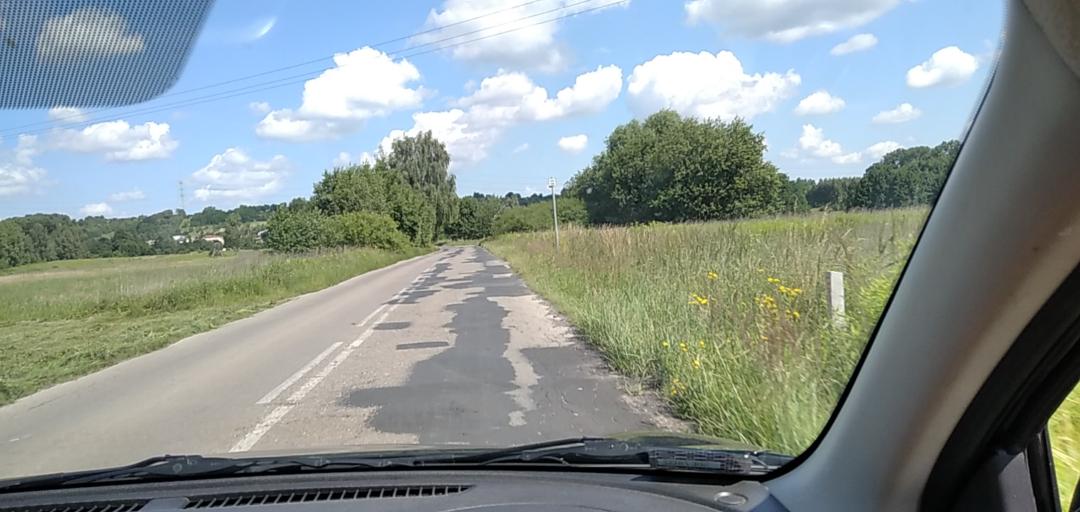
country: PL
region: Silesian Voivodeship
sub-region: Powiat bedzinski
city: Sarnow
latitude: 50.3979
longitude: 19.1380
